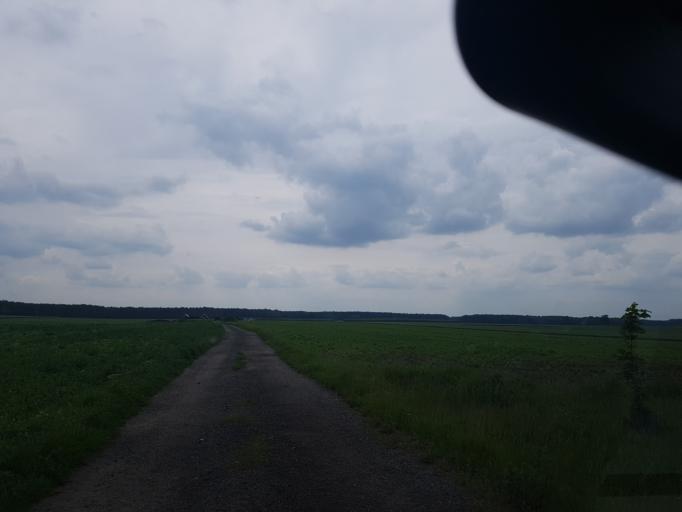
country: DE
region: Brandenburg
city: Finsterwalde
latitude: 51.5645
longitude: 13.6652
